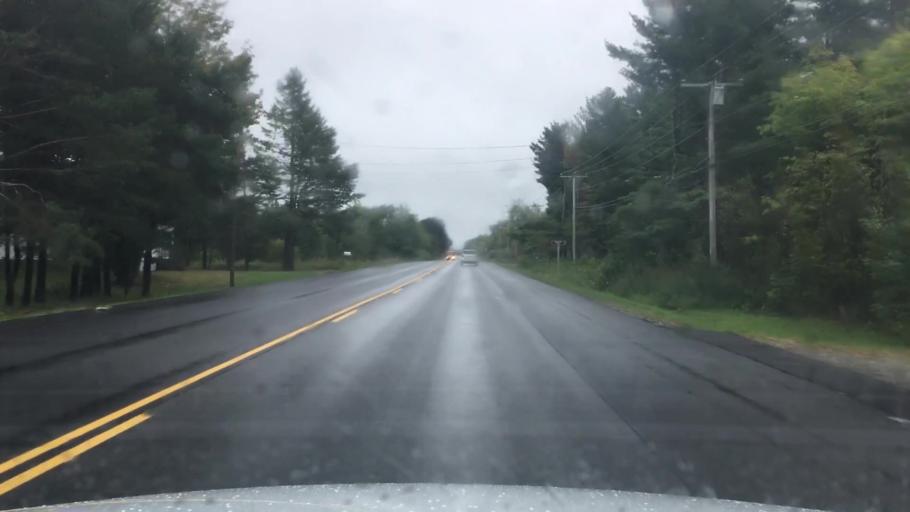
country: US
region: Maine
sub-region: Penobscot County
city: Hampden
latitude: 44.7622
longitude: -68.8493
